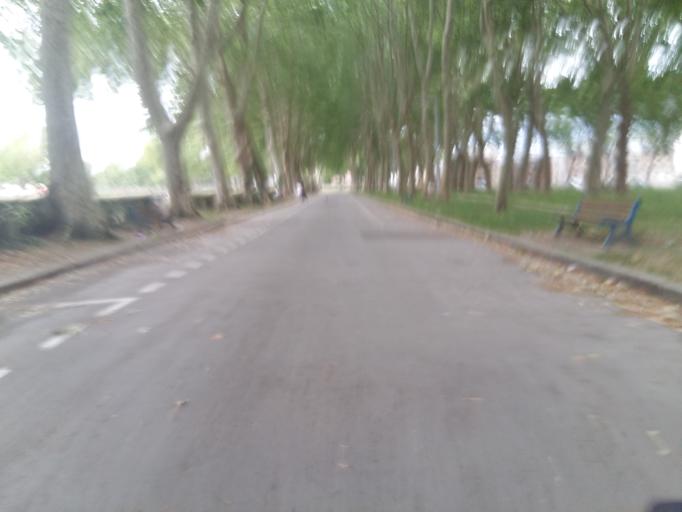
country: FR
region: Picardie
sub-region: Departement de la Somme
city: Amiens
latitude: 49.8981
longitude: 2.2857
